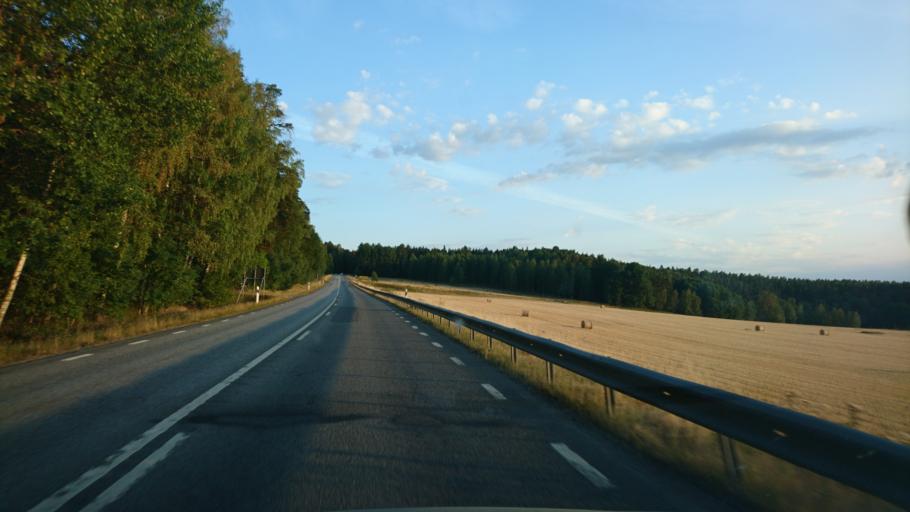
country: SE
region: Uppsala
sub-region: Uppsala Kommun
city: Saevja
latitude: 59.7824
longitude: 17.6642
